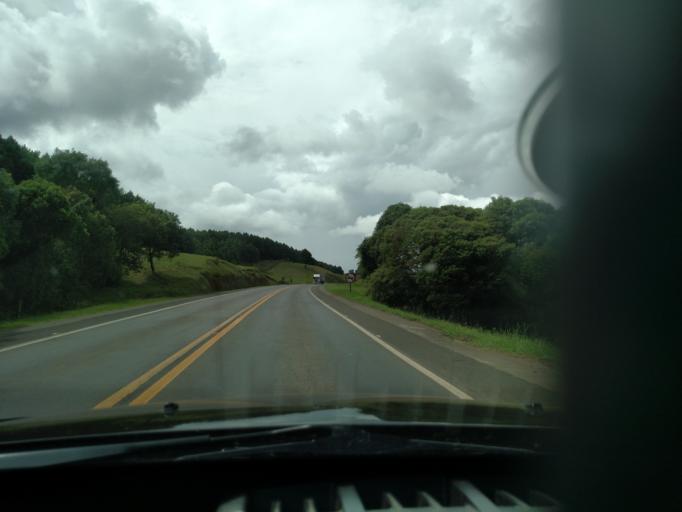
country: BR
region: Santa Catarina
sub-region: Lages
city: Lages
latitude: -27.8282
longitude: -50.3803
